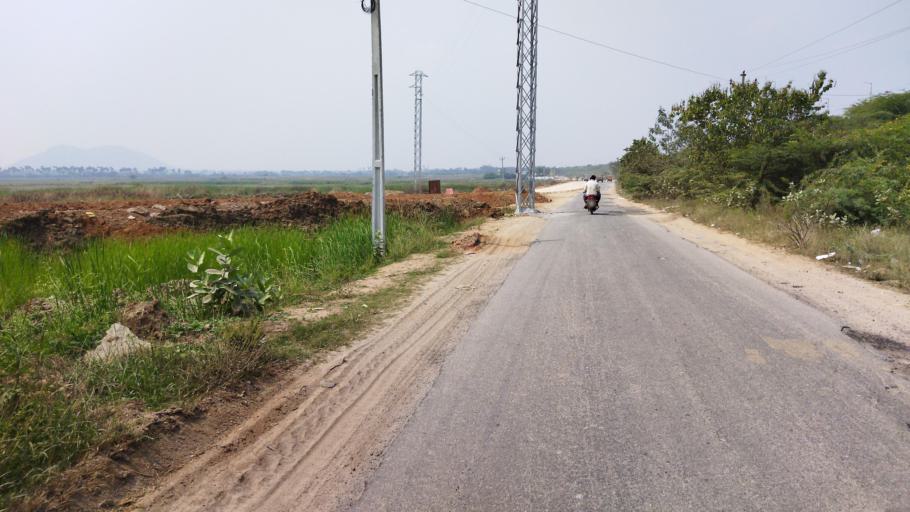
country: IN
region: Telangana
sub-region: Nalgonda
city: Nalgonda
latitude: 17.0777
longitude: 79.3110
